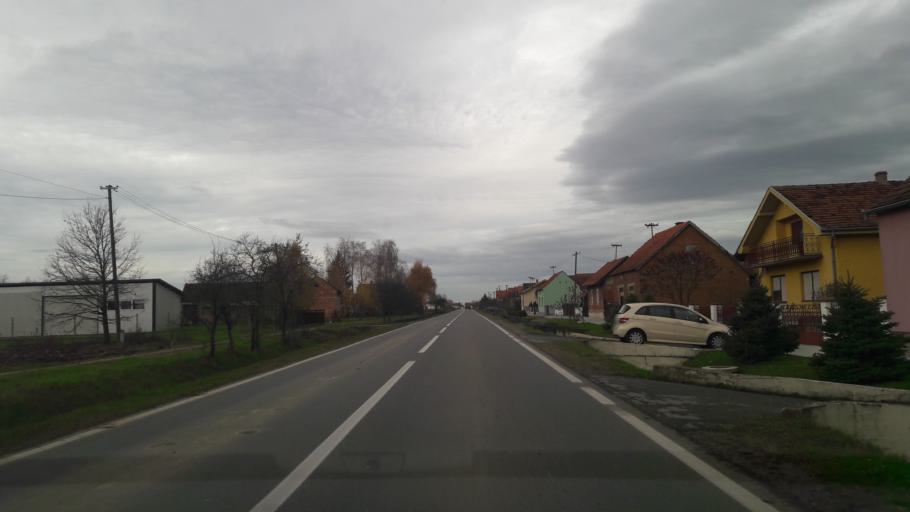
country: HR
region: Osjecko-Baranjska
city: Fericanci
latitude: 45.5284
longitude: 17.9563
